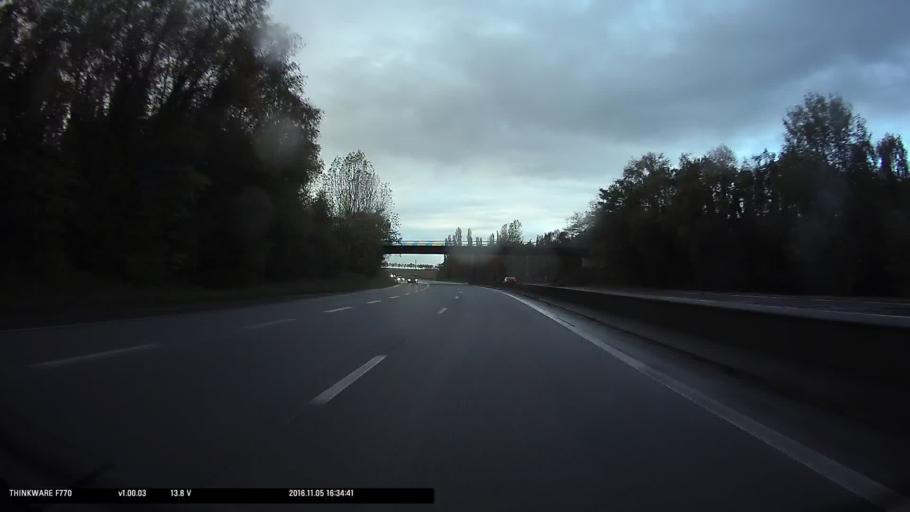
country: FR
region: Ile-de-France
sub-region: Departement du Val-d'Oise
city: Ableiges
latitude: 49.0710
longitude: 1.9663
